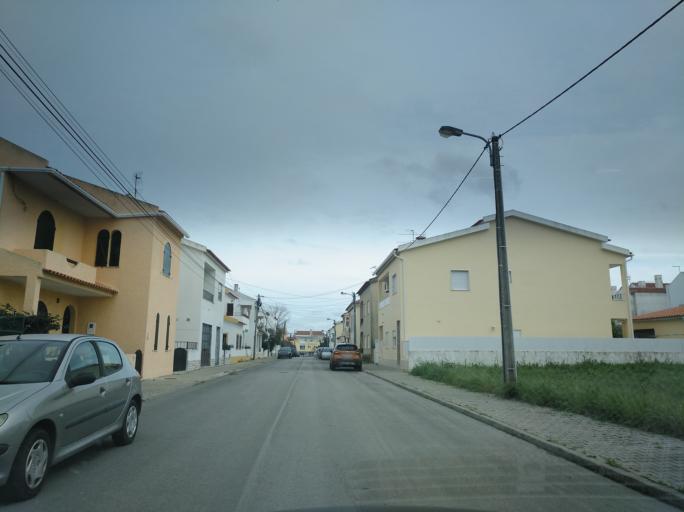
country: PT
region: Setubal
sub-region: Grandola
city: Grandola
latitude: 38.1826
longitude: -8.5696
